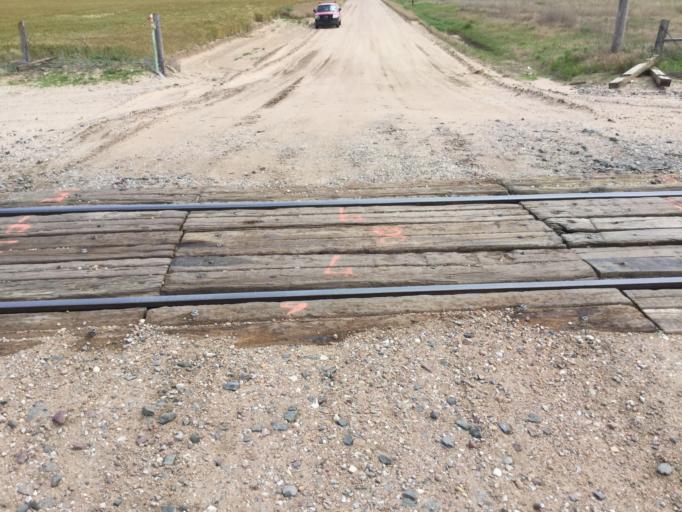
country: US
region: Kansas
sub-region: Edwards County
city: Kinsley
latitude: 37.9349
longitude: -99.3141
